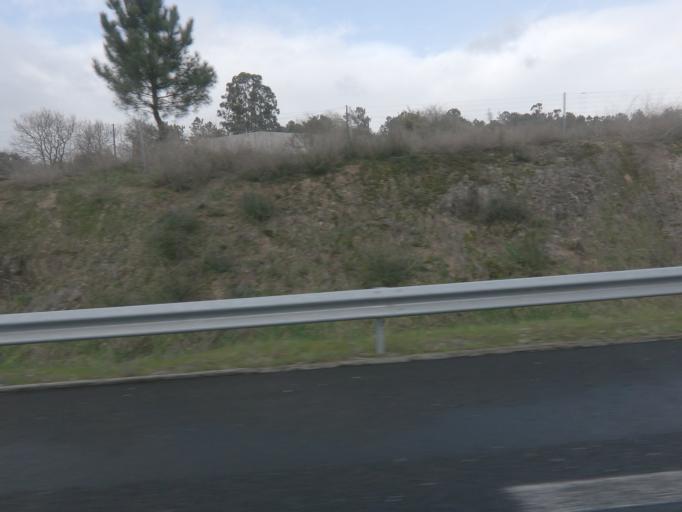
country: ES
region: Galicia
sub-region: Provincia da Coruna
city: Ribeira
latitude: 42.7480
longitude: -8.3867
